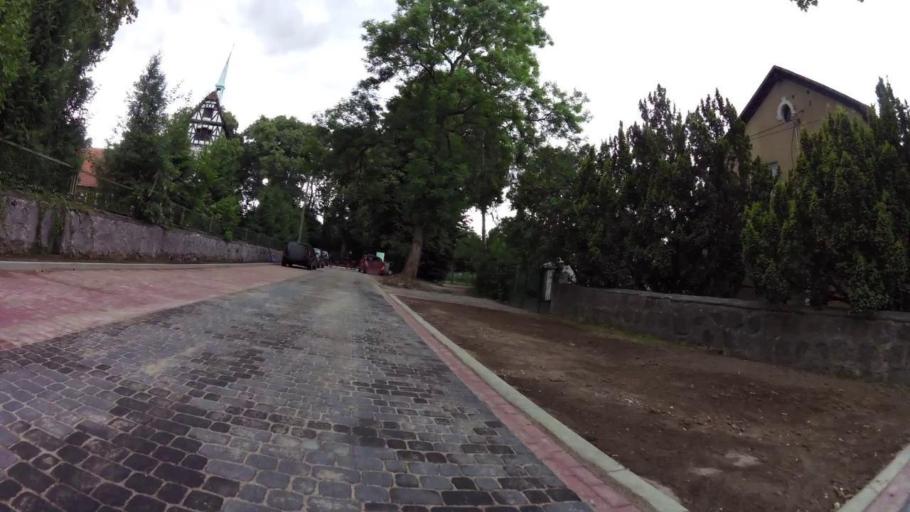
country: PL
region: West Pomeranian Voivodeship
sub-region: Powiat lobeski
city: Resko
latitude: 53.7601
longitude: 15.5307
